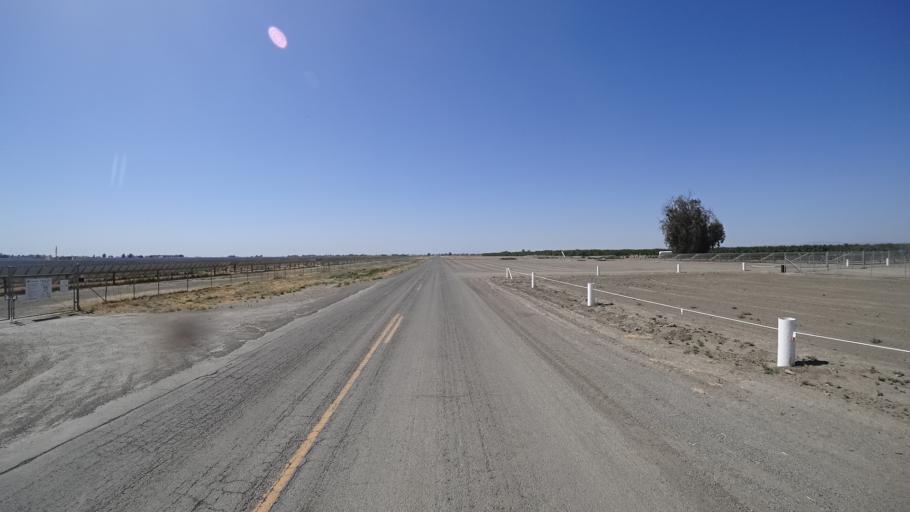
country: US
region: California
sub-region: Kings County
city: Stratford
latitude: 36.2253
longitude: -119.8341
